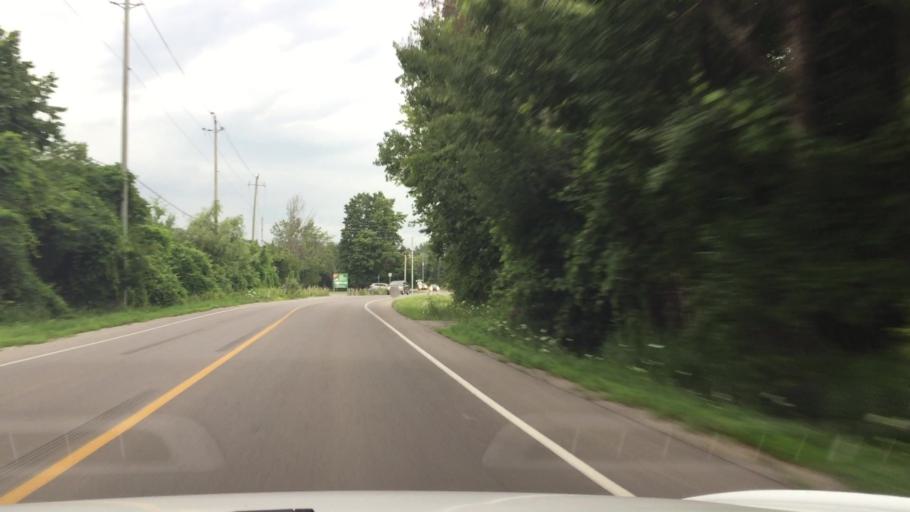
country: CA
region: Ontario
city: Oshawa
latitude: 43.9308
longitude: -78.7974
